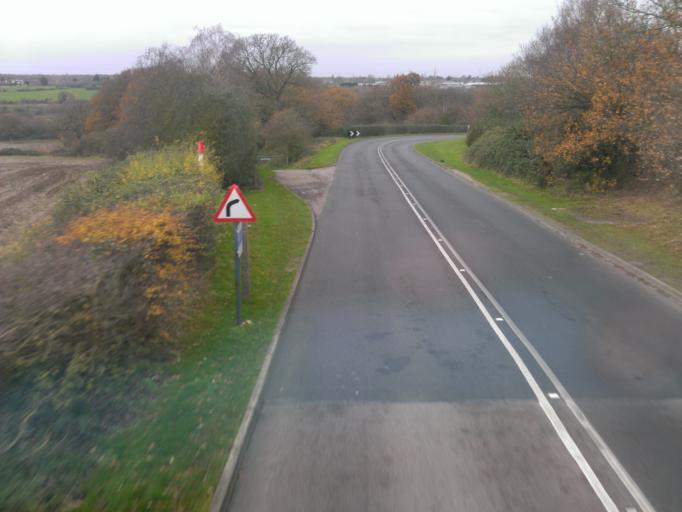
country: GB
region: England
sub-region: Essex
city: Rowhedge
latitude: 51.8733
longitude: 0.9450
